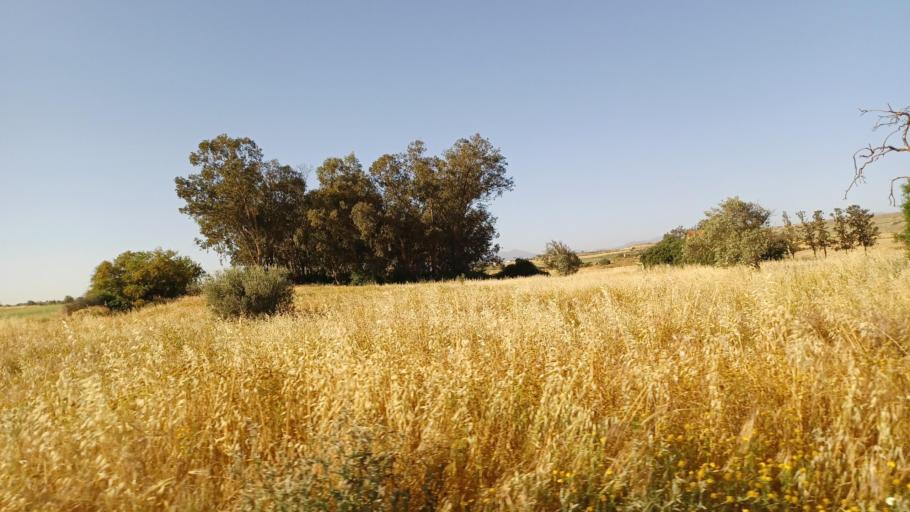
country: CY
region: Lefkosia
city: Mammari
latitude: 35.1704
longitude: 33.2482
